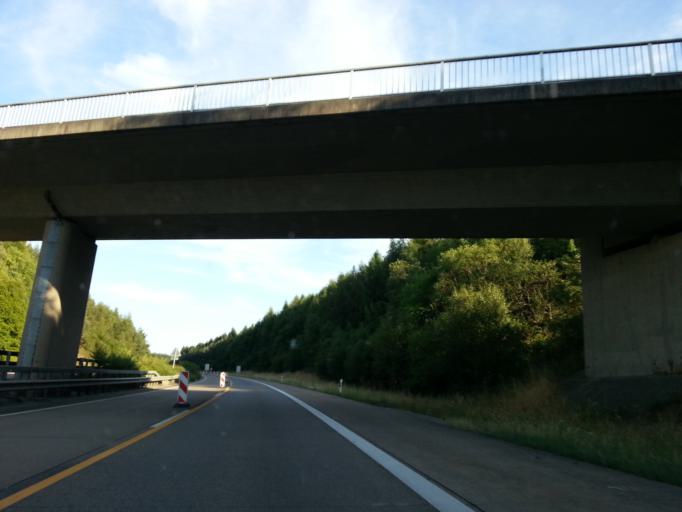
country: DE
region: Rheinland-Pfalz
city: Bescheid
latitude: 49.7430
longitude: 6.8761
